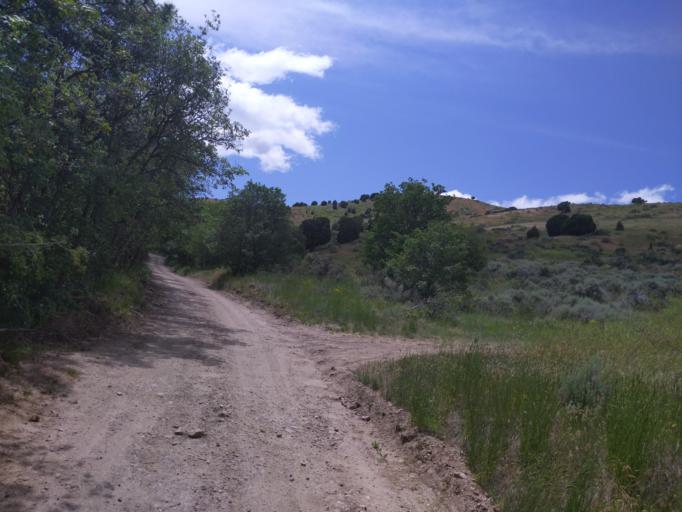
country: US
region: Idaho
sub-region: Bannock County
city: Pocatello
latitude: 42.8355
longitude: -112.4736
